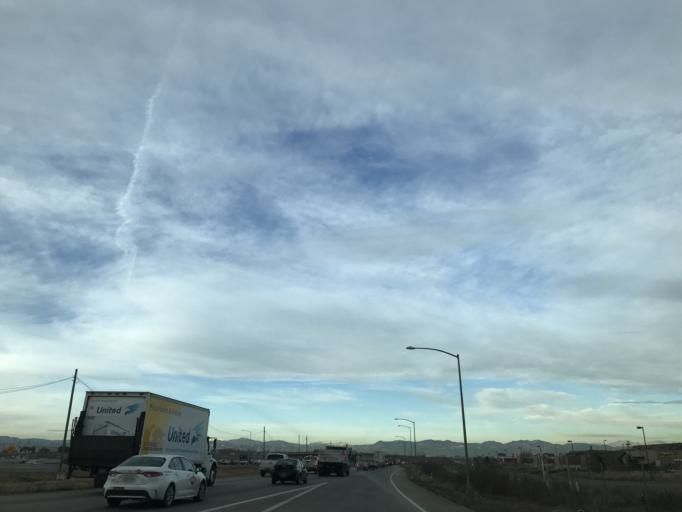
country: US
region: Colorado
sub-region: Adams County
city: Commerce City
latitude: 39.7787
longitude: -104.8890
